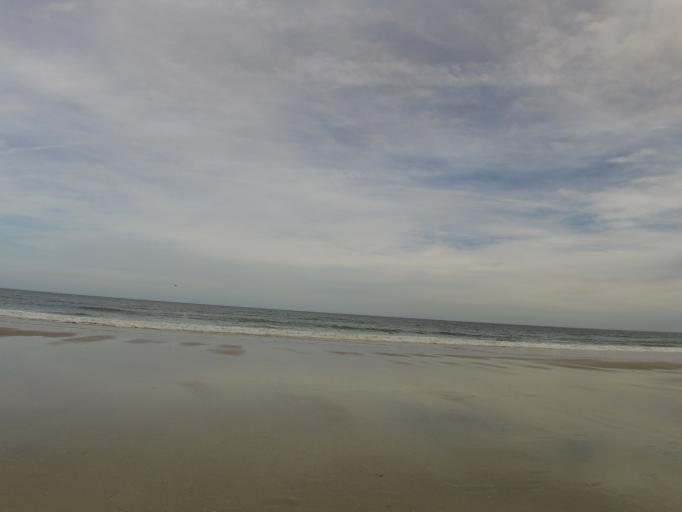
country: US
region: Florida
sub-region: Saint Johns County
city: Villano Beach
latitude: 29.9268
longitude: -81.2945
